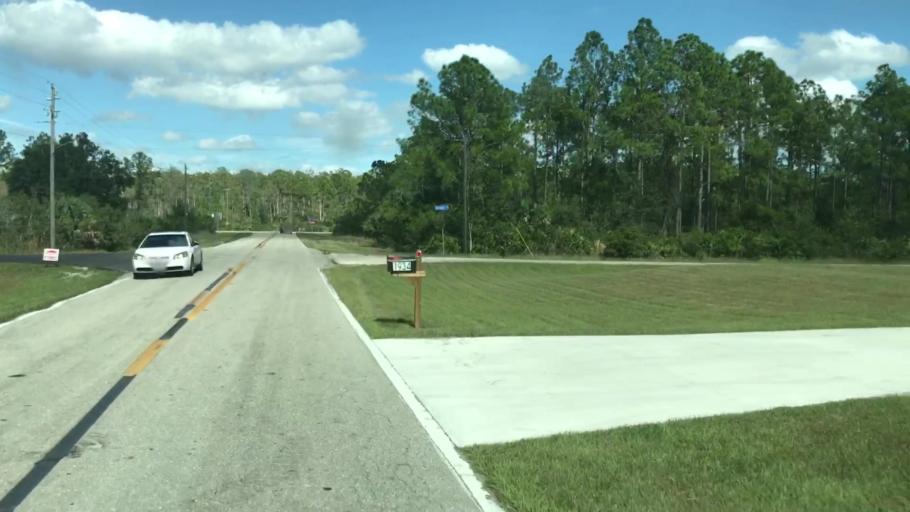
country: US
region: Florida
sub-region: Lee County
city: Alva
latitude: 26.6767
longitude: -81.6248
